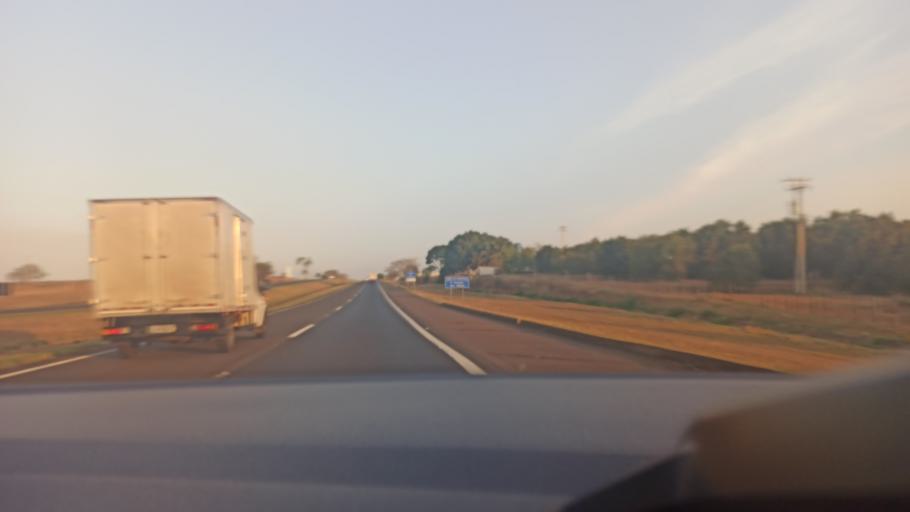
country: BR
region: Sao Paulo
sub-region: Santa Adelia
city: Santa Adelia
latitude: -21.3734
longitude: -48.7462
